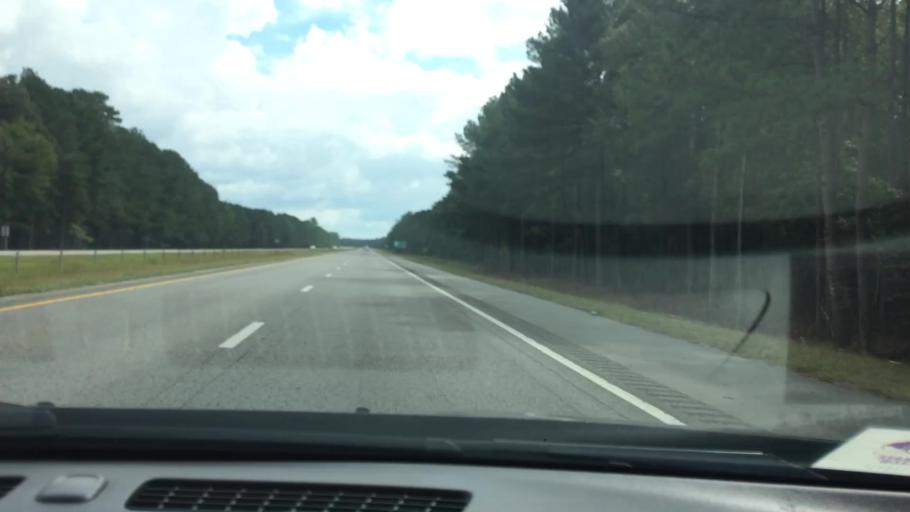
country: US
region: North Carolina
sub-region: Pitt County
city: Farmville
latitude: 35.6372
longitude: -77.7249
